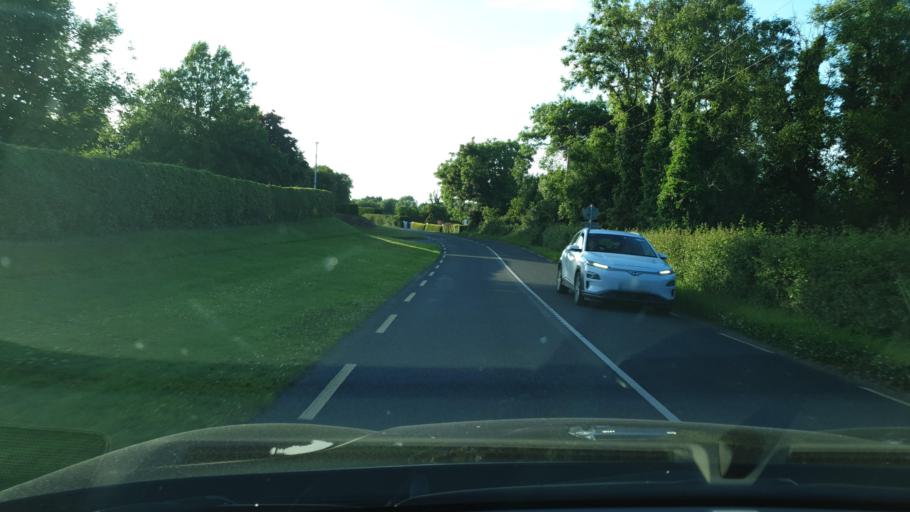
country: IE
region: Leinster
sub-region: An Mhi
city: Ratoath
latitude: 53.4998
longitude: -6.4413
